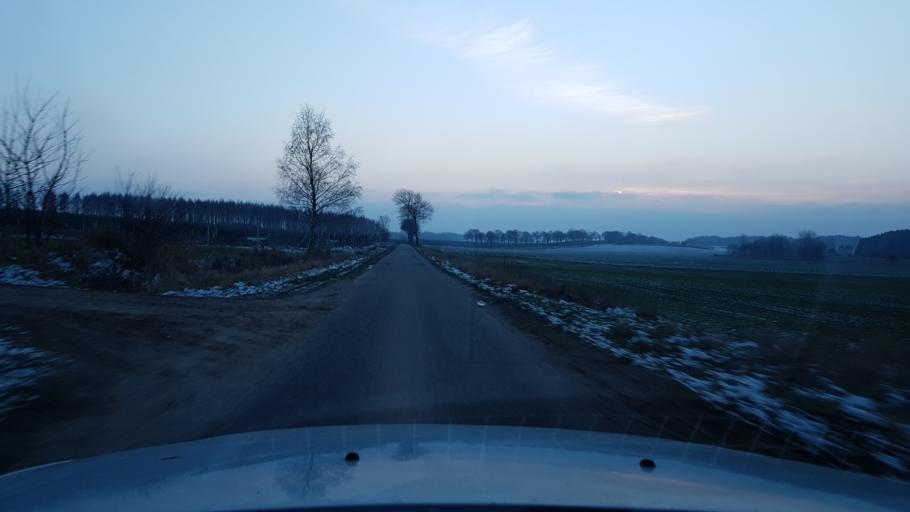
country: PL
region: West Pomeranian Voivodeship
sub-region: Powiat bialogardzki
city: Karlino
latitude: 53.9809
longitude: 15.7948
